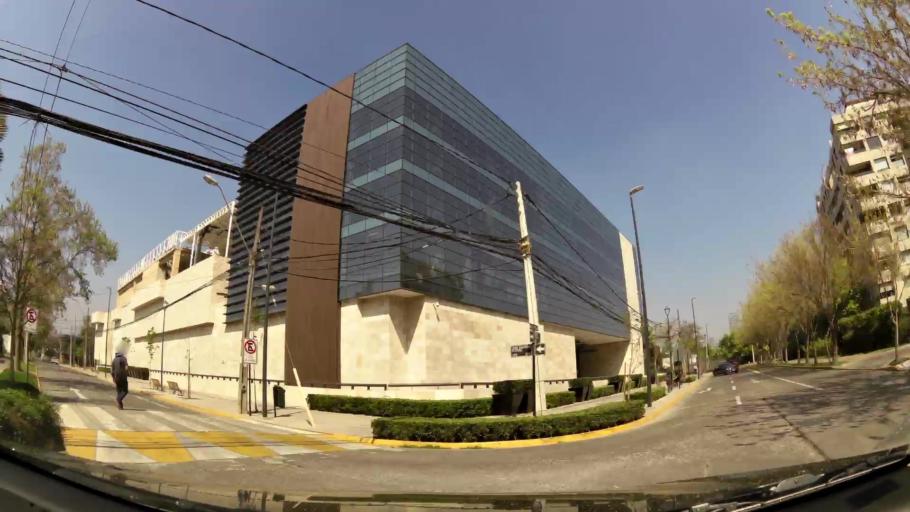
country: CL
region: Santiago Metropolitan
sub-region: Provincia de Santiago
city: Villa Presidente Frei, Nunoa, Santiago, Chile
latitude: -33.3979
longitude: -70.5992
